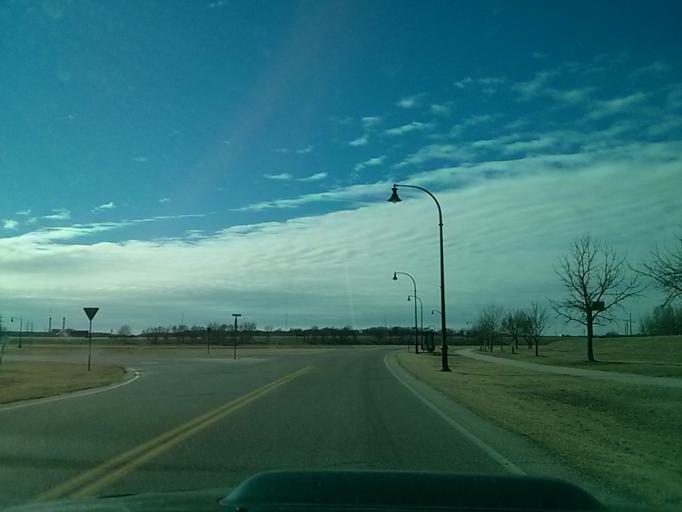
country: US
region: Oklahoma
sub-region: Tulsa County
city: Jenks
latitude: 36.0205
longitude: -95.9589
